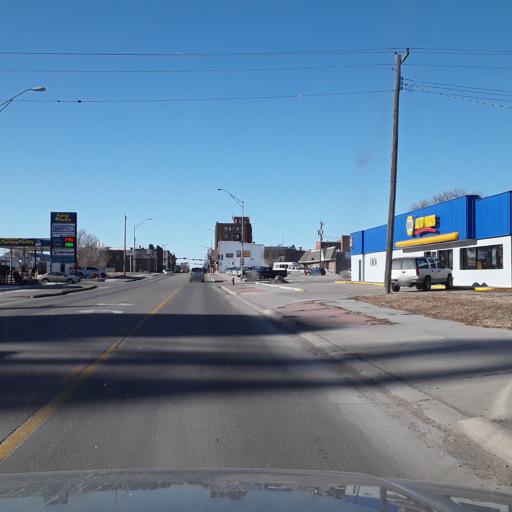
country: US
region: Nebraska
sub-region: Phelps County
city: Holdrege
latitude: 40.4381
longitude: -99.3659
